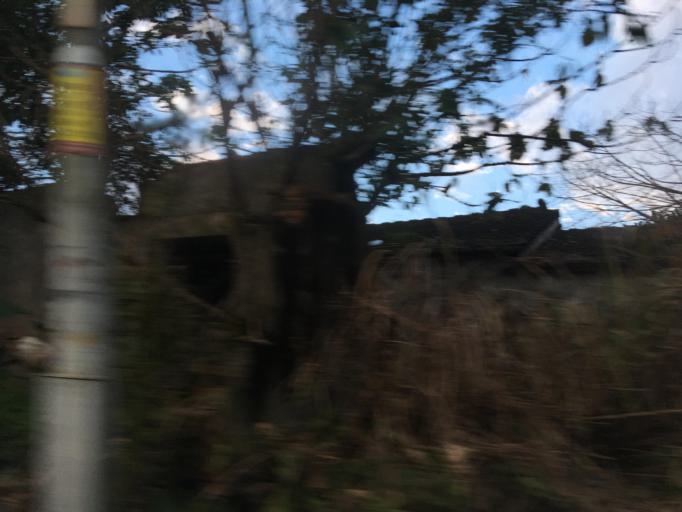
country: TW
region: Taiwan
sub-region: Yilan
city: Yilan
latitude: 24.7498
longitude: 121.7244
